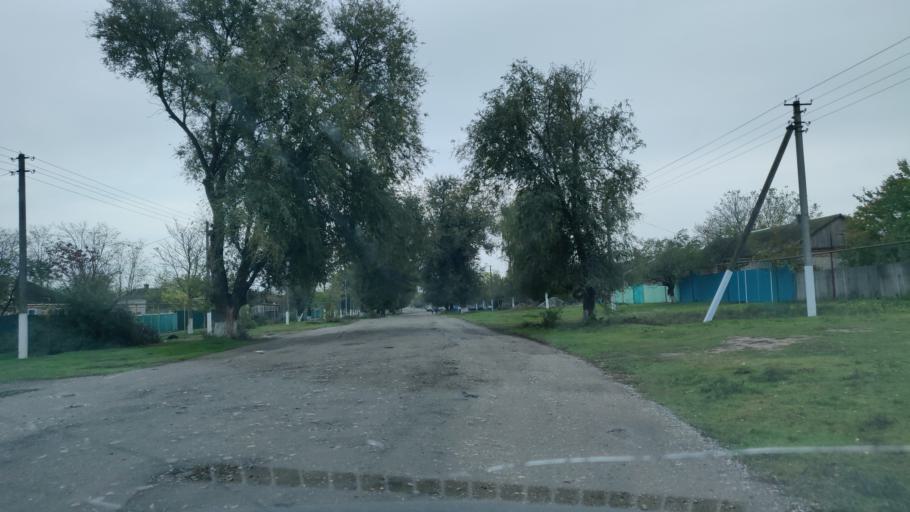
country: RU
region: Stavropol'skiy
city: Irgakly
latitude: 44.2416
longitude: 44.7219
